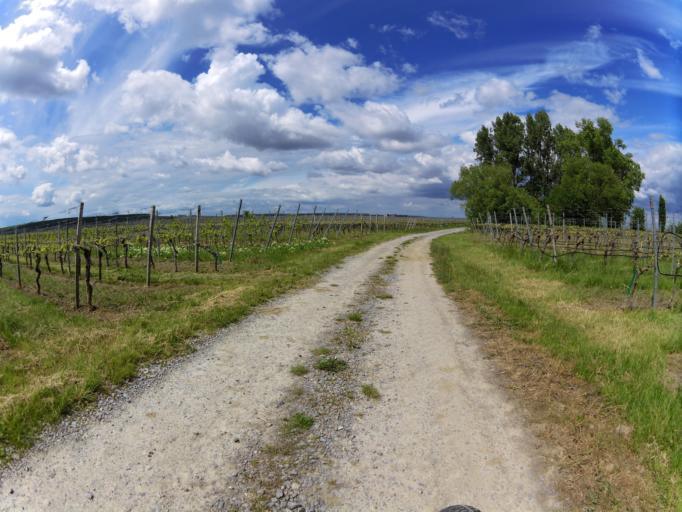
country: DE
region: Bavaria
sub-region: Regierungsbezirk Unterfranken
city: Sommerach
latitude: 49.8450
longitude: 10.1910
